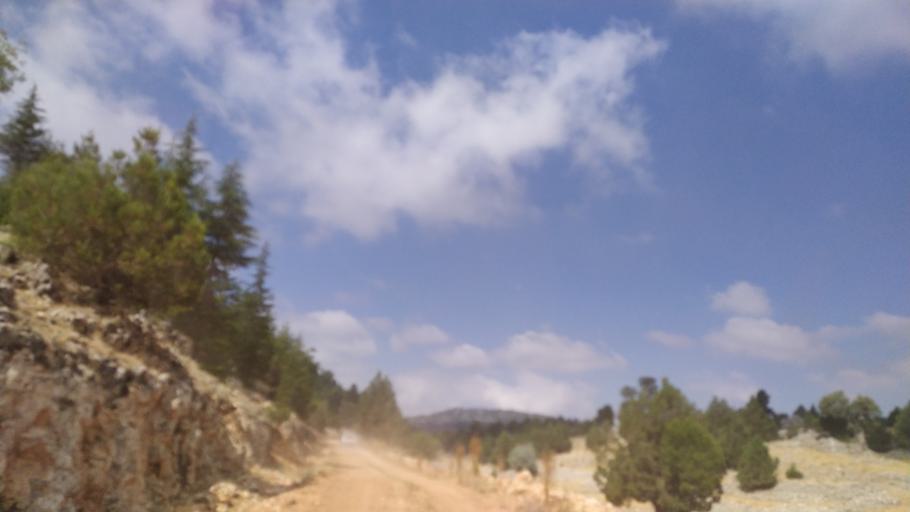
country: TR
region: Mersin
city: Kirobasi
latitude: 36.6175
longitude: 33.8352
